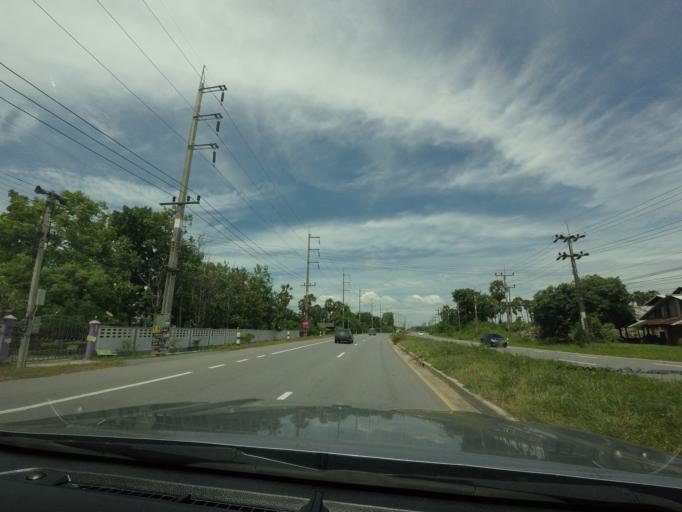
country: TH
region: Songkhla
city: Ranot
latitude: 7.7191
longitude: 100.3703
